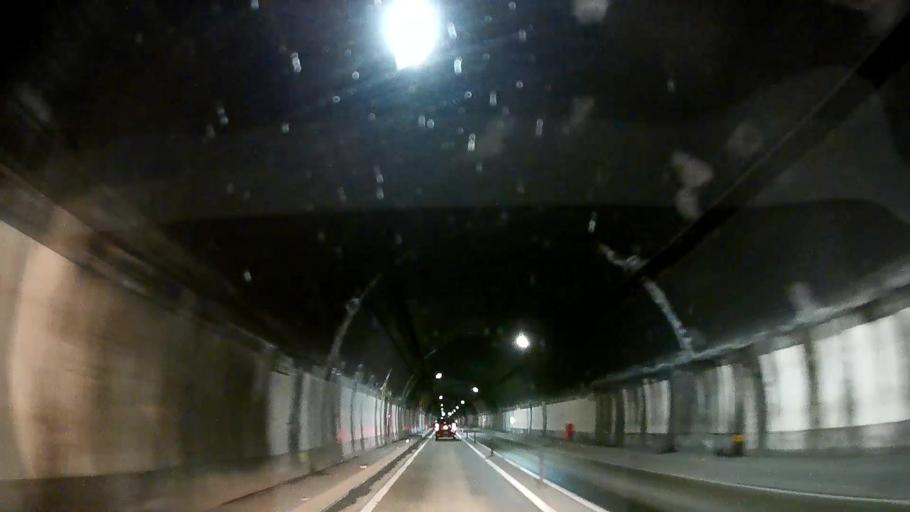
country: JP
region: Saitama
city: Chichibu
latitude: 35.9512
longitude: 139.1758
